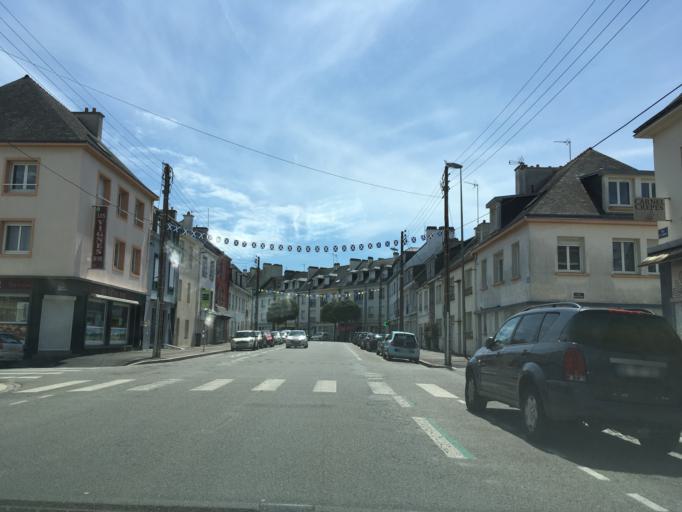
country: FR
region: Brittany
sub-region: Departement du Morbihan
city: Lorient
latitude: 47.7399
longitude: -3.3688
